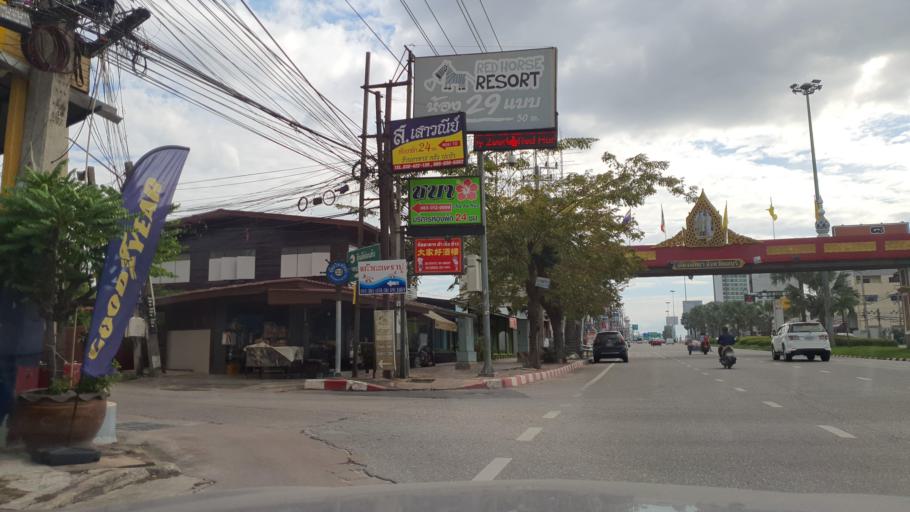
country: TH
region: Chon Buri
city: Phatthaya
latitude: 12.9600
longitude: 100.9089
